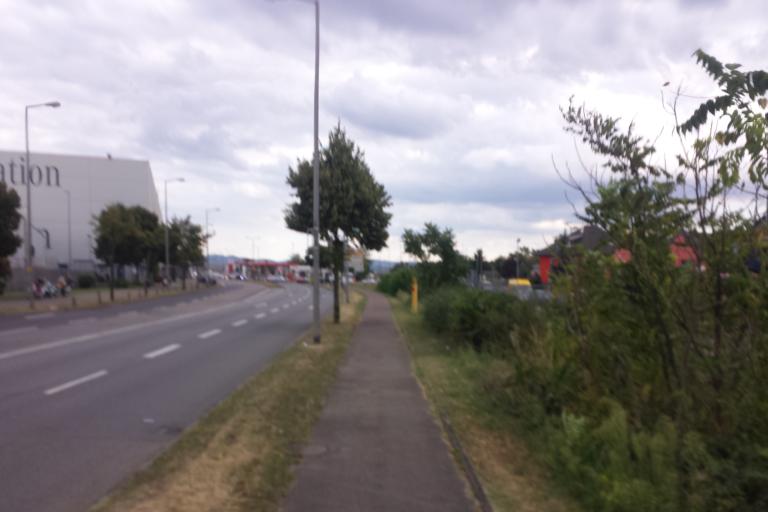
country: DE
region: Baden-Wuerttemberg
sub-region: Karlsruhe Region
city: Mannheim
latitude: 49.5140
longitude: 8.4803
